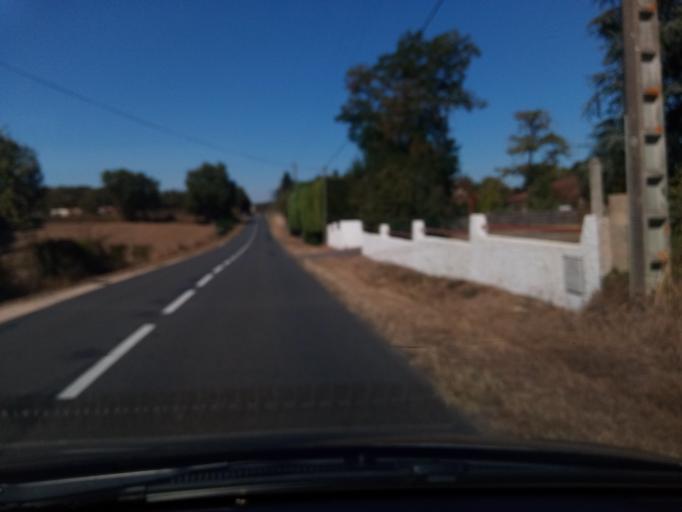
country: FR
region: Poitou-Charentes
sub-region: Departement de la Vienne
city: Montmorillon
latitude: 46.4867
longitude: 0.8450
